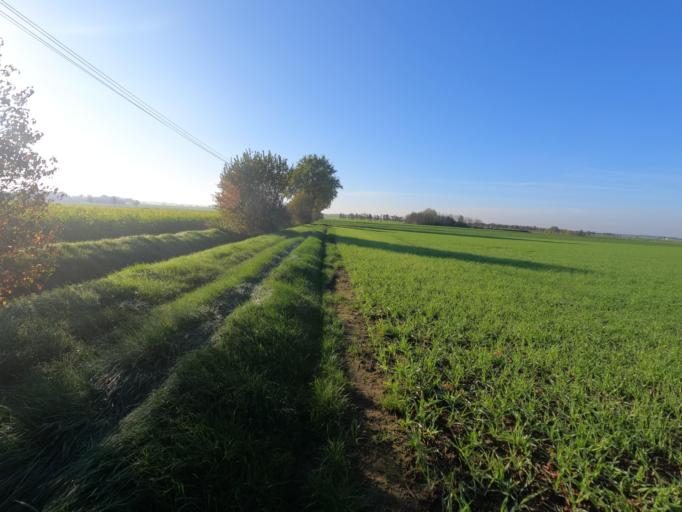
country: DE
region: North Rhine-Westphalia
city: Erkelenz
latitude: 51.0831
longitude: 6.3828
